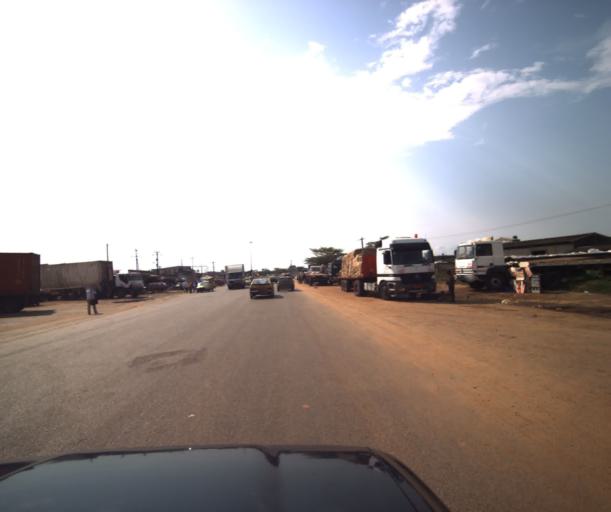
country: CM
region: Littoral
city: Douala
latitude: 4.0185
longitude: 9.7243
